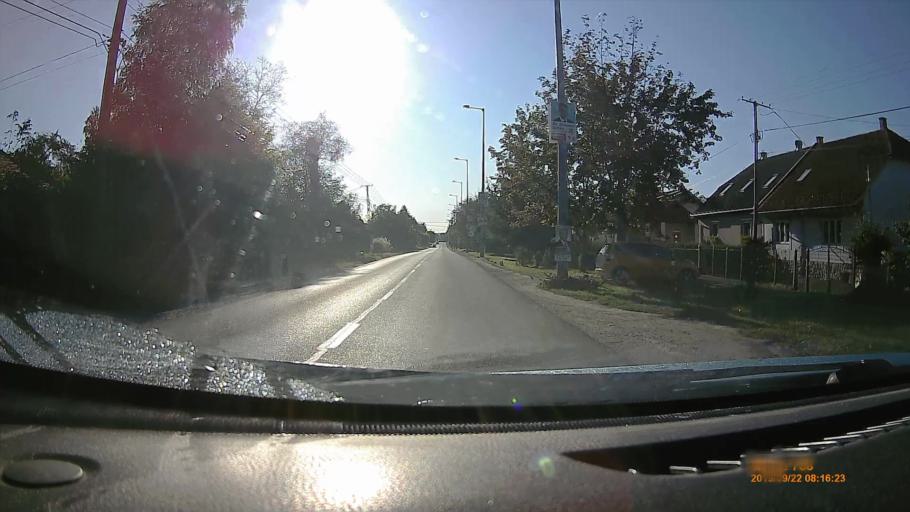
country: HU
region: Borsod-Abauj-Zemplen
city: Sajobabony
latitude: 48.1135
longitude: 20.6646
